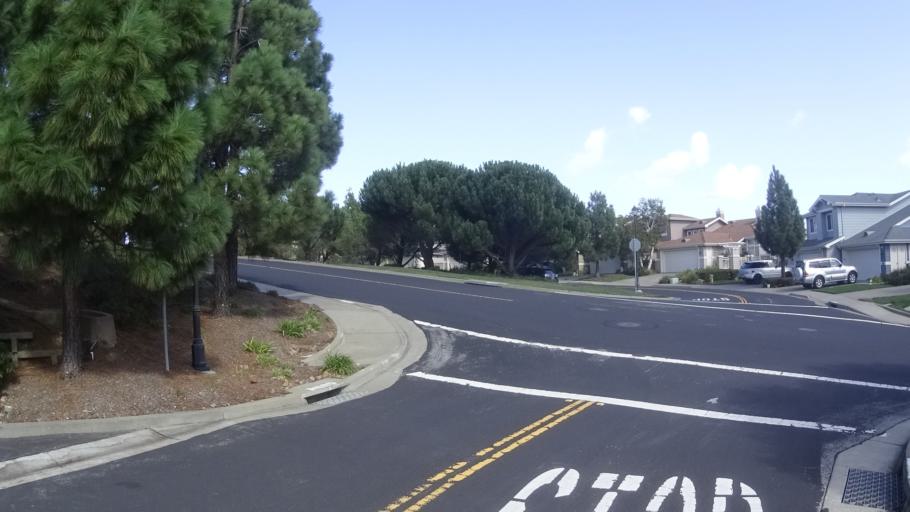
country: US
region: California
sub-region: San Mateo County
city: Brisbane
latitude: 37.6929
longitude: -122.4096
